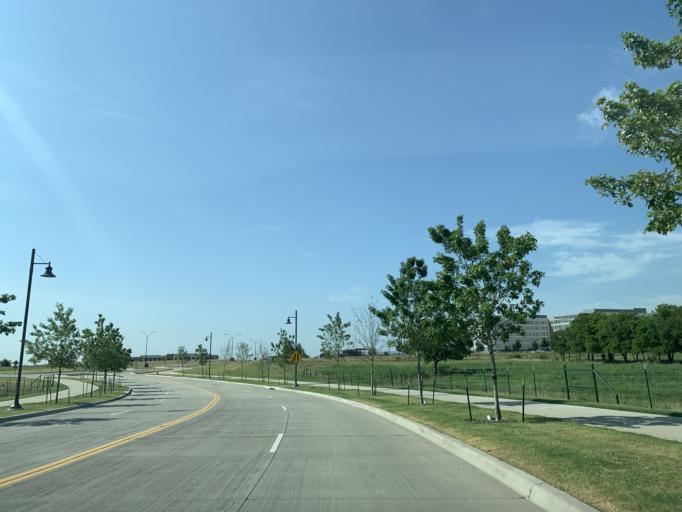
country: US
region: Texas
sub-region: Tarrant County
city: Haslet
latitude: 32.9246
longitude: -97.3127
